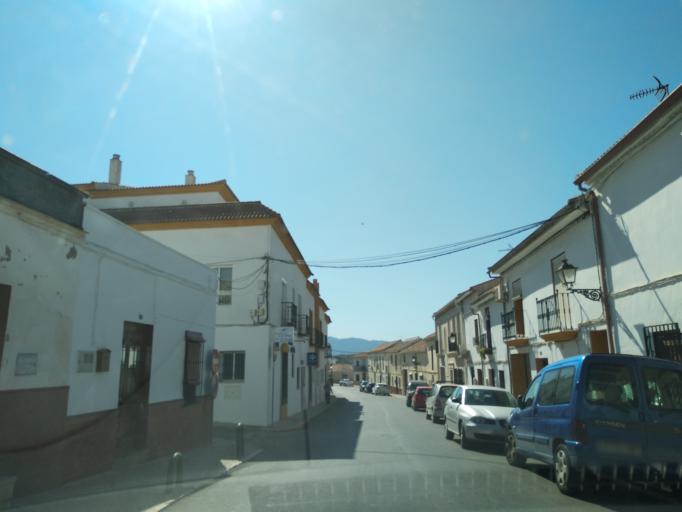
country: ES
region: Andalusia
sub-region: Provincia de Malaga
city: Mollina
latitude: 37.1248
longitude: -4.6569
